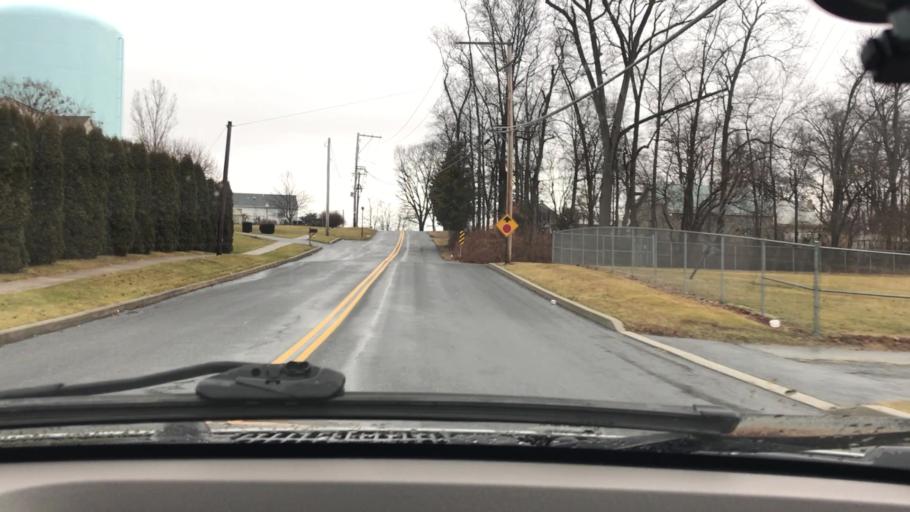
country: US
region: Pennsylvania
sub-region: Lancaster County
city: Elizabethtown
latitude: 40.1704
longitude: -76.5982
